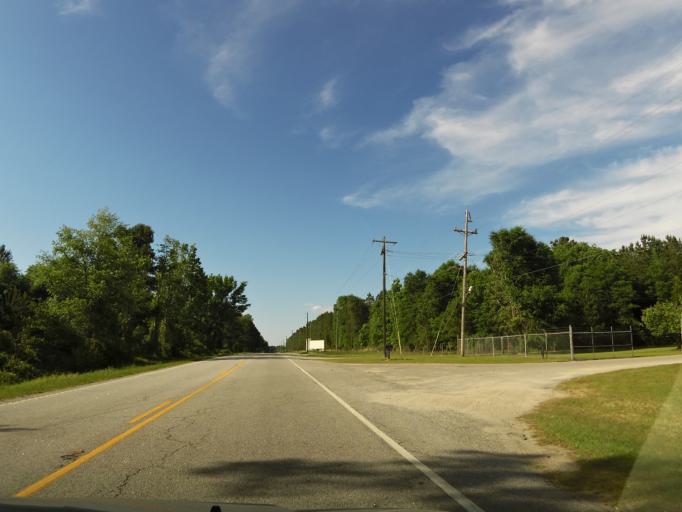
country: US
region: South Carolina
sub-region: Allendale County
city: Fairfax
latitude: 32.9258
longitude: -81.2373
